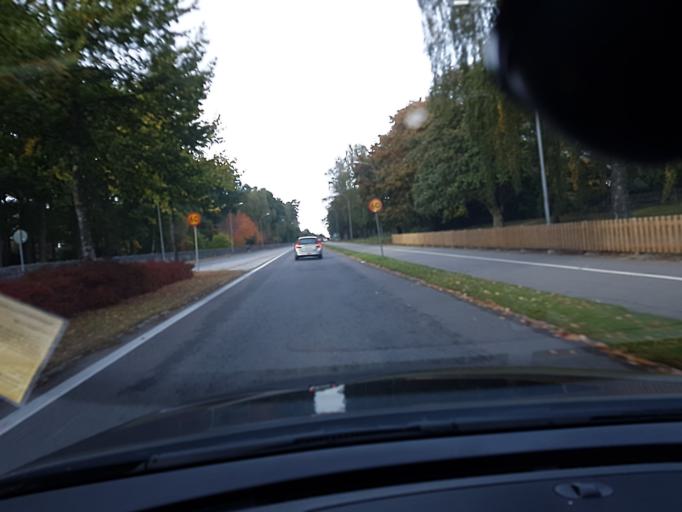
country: SE
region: Kronoberg
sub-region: Vaxjo Kommun
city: Vaexjoe
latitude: 56.8872
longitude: 14.8141
